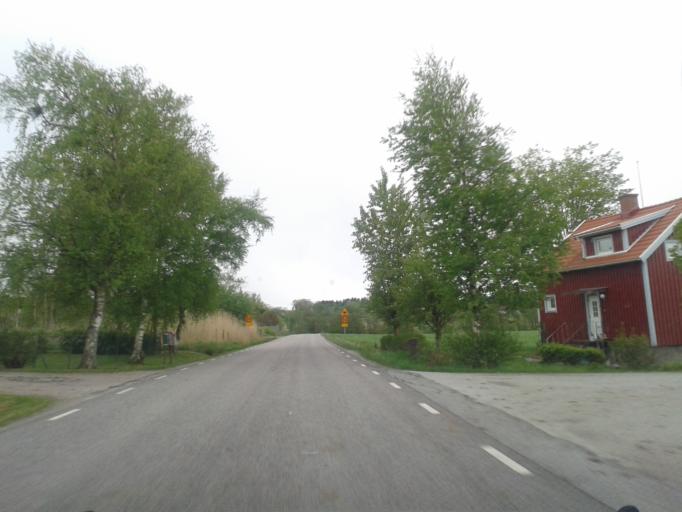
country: SE
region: Vaestra Goetaland
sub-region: Kungalvs Kommun
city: Kode
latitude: 57.9464
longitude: 11.8197
